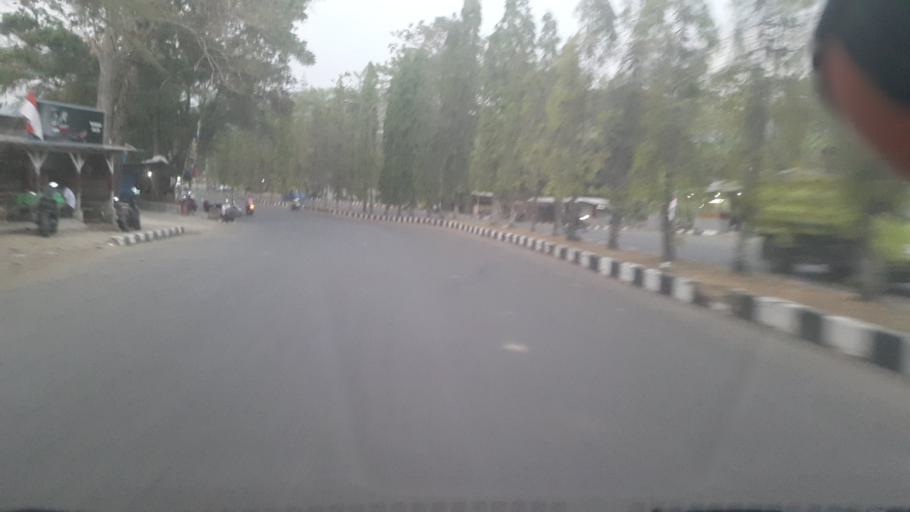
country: ID
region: West Java
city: Pelabuhanratu
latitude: -6.9952
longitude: 106.5579
